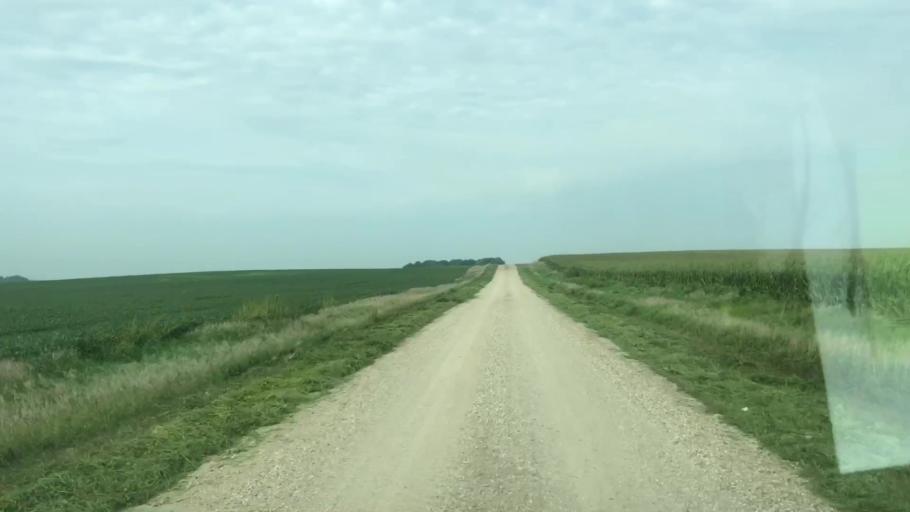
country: US
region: Iowa
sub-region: O'Brien County
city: Sheldon
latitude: 43.2720
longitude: -95.8620
